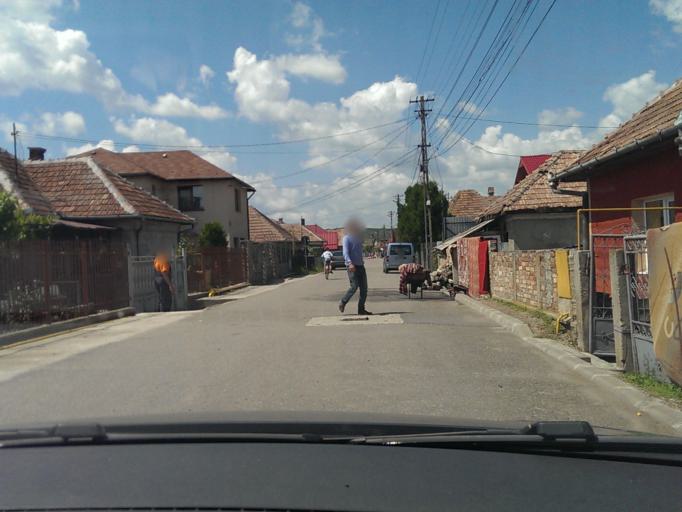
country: RO
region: Cluj
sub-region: Comuna Apahida
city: Sannicoara
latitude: 46.7957
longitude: 23.7441
